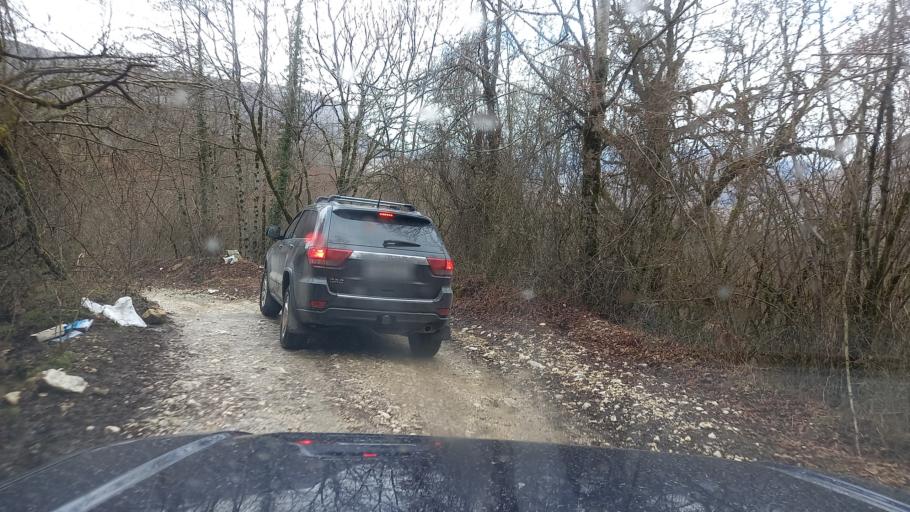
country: GE
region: Abkhazia
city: Dranda
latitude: 43.0360
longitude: 41.3226
